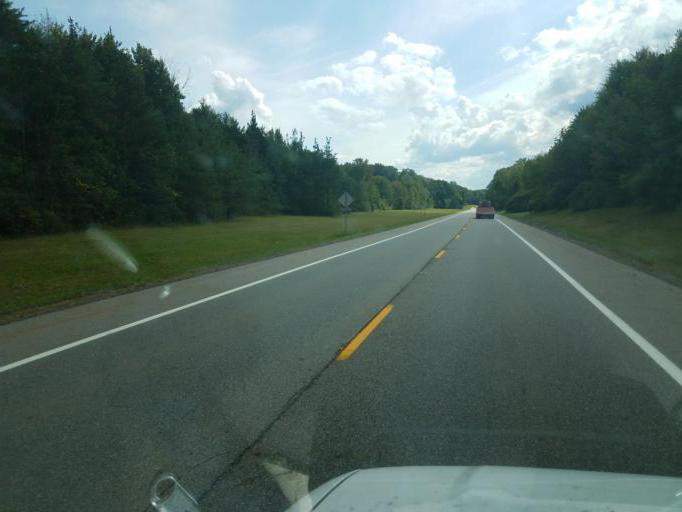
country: US
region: Ohio
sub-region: Portage County
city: Ravenna
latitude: 41.1356
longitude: -81.2283
